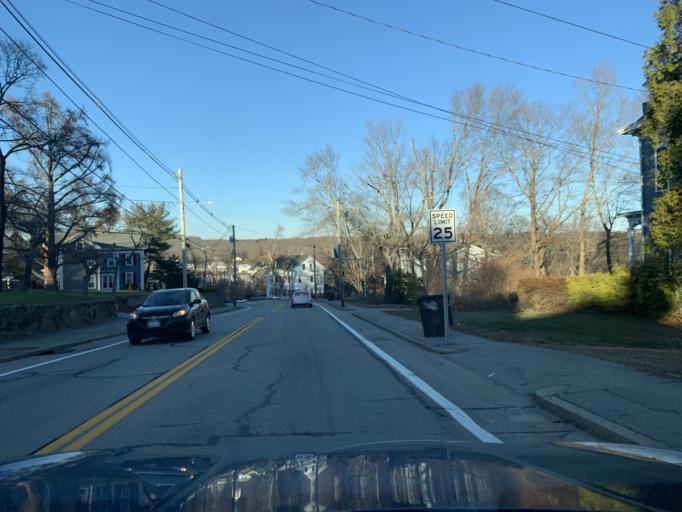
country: US
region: Rhode Island
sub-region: Kent County
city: West Warwick
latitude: 41.7183
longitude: -71.5327
